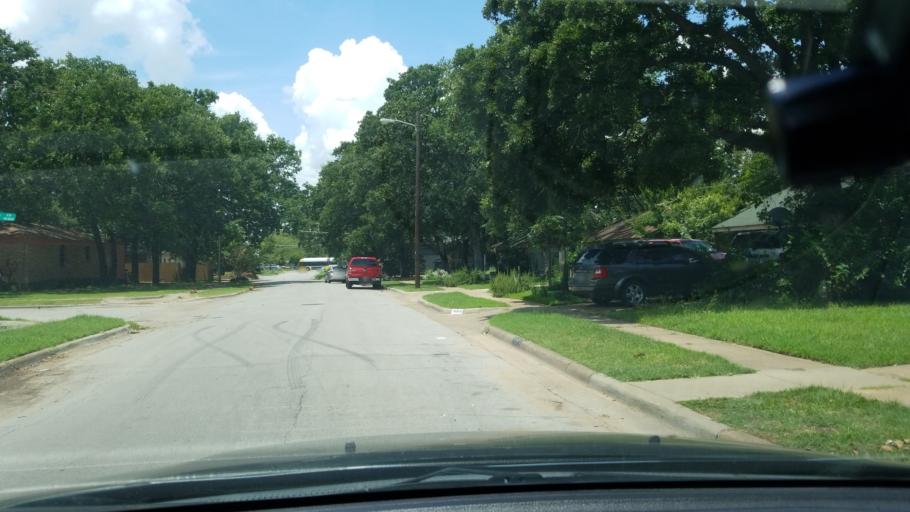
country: US
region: Texas
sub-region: Dallas County
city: Balch Springs
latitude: 32.7382
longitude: -96.6464
